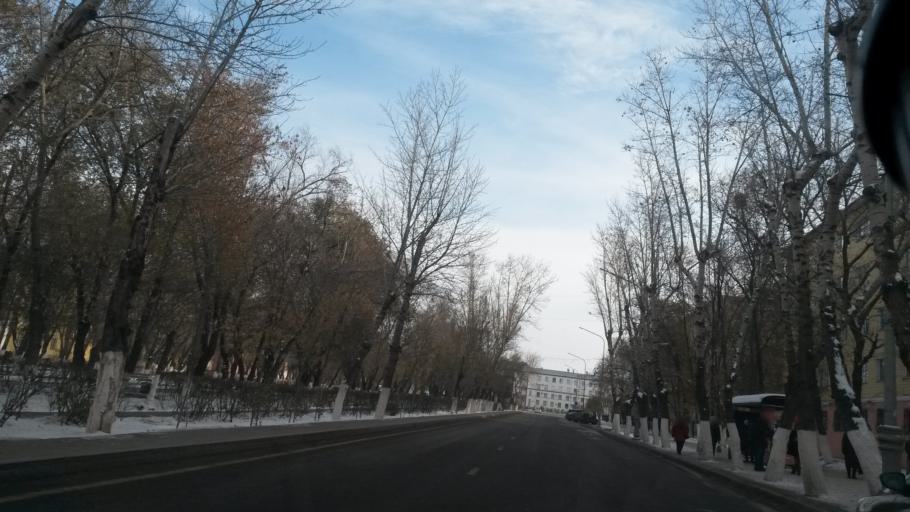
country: KZ
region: Qaraghandy
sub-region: Qaraghandy Qalasy
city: Karagandy
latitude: 49.8168
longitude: 73.0997
